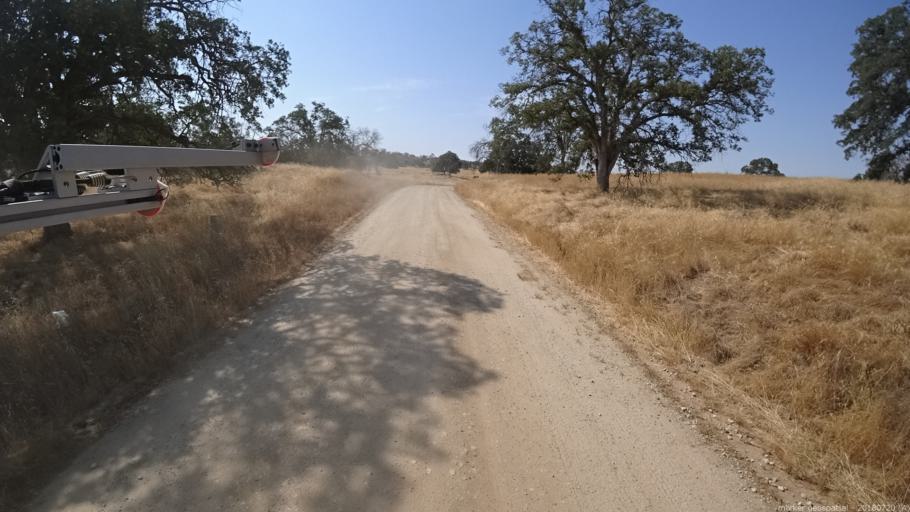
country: US
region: California
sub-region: Madera County
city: Yosemite Lakes
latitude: 37.2440
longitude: -119.9136
